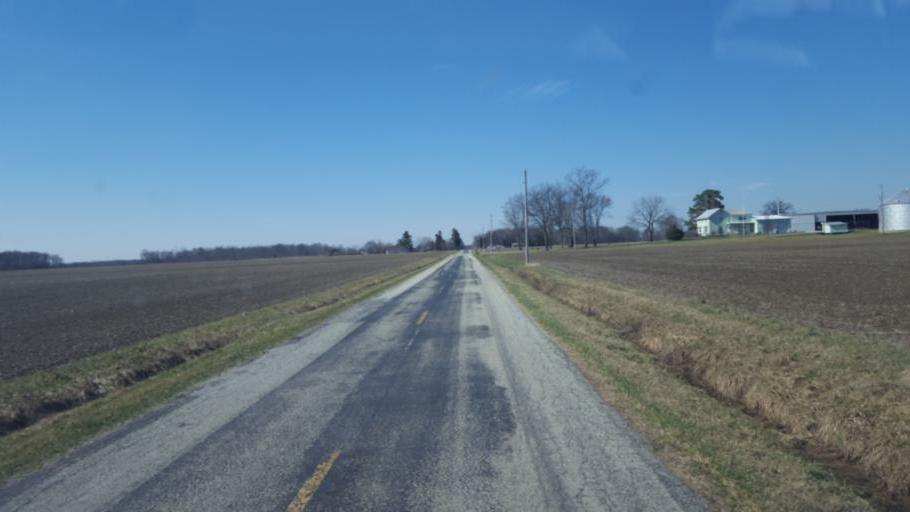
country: US
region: Ohio
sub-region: Delaware County
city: Ashley
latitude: 40.4920
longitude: -82.9821
